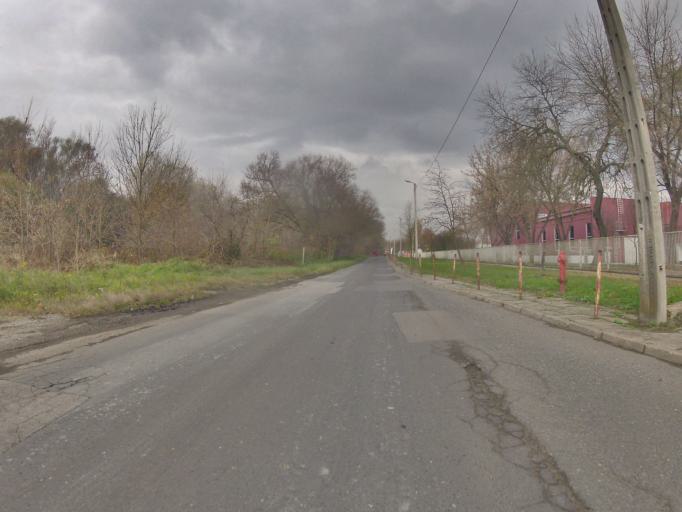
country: PL
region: Lesser Poland Voivodeship
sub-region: Powiat wielicki
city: Wegrzce Wielkie
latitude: 50.0532
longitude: 20.1018
